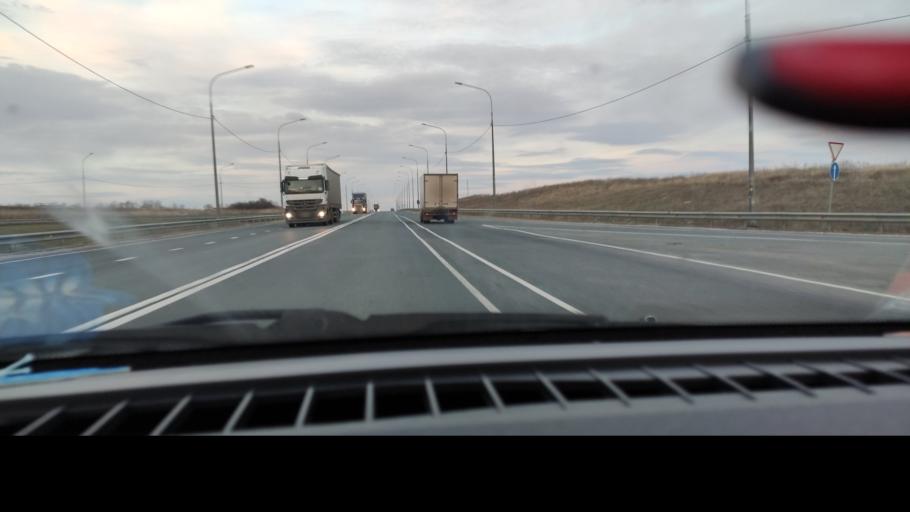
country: RU
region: Saratov
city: Yelshanka
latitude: 51.8307
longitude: 46.4320
